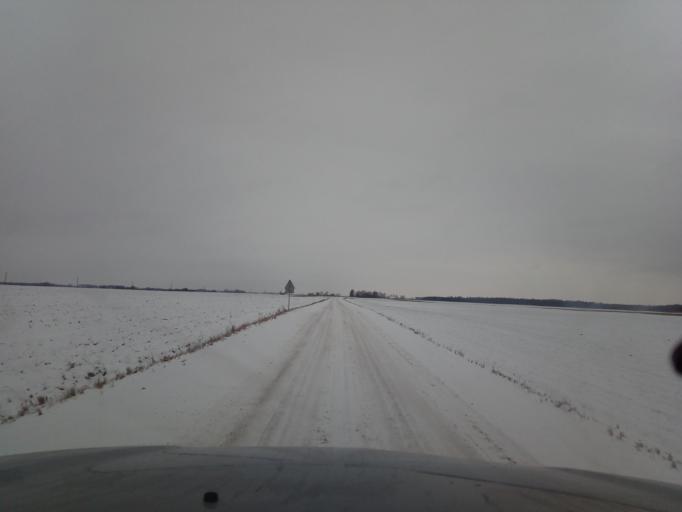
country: LT
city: Ramygala
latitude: 55.4918
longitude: 24.5515
